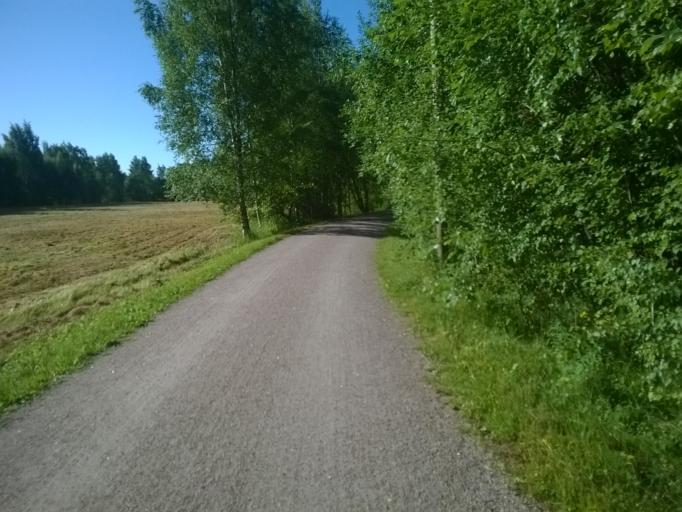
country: FI
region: Uusimaa
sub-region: Helsinki
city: Helsinki
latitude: 60.2444
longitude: 24.9078
